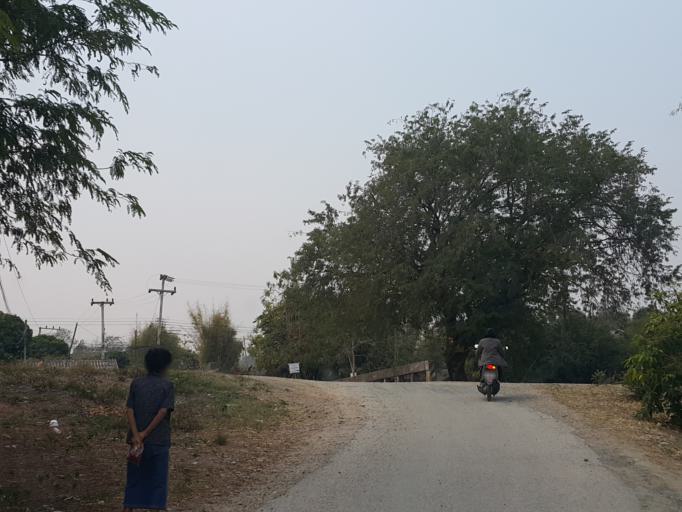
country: TH
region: Chiang Mai
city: Mae Taeng
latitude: 18.9665
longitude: 98.9430
